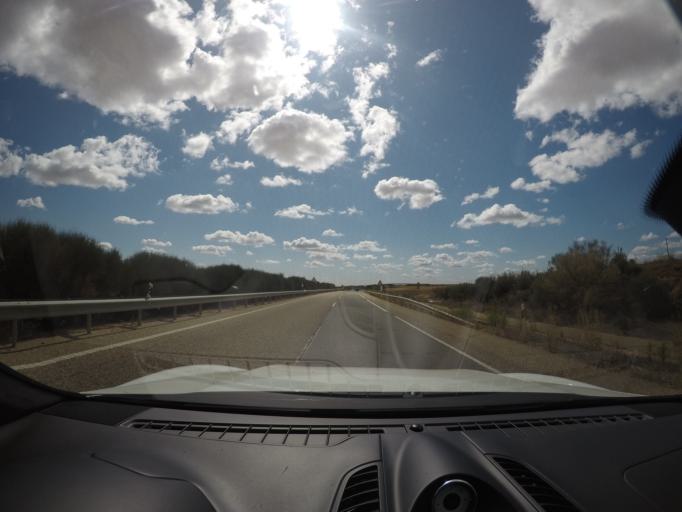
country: ES
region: Castille and Leon
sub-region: Provincia de Zamora
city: Matilla de Arzon
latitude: 42.0820
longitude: -5.6553
